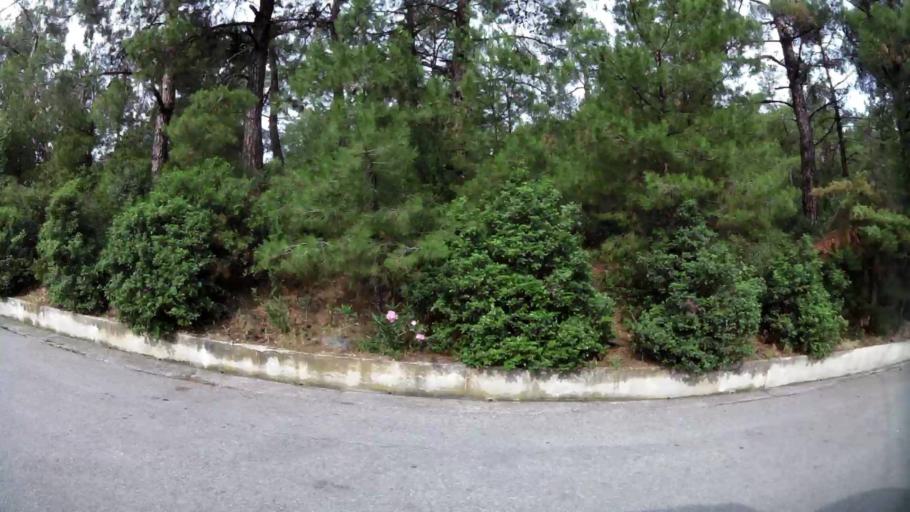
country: GR
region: Central Macedonia
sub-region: Nomos Thessalonikis
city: Panorama
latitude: 40.5873
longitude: 23.0333
